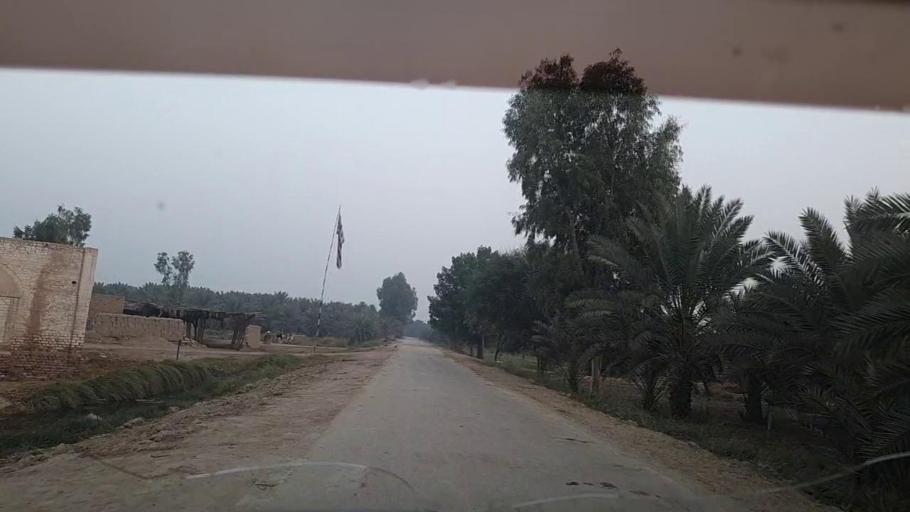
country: PK
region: Sindh
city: Khairpur
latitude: 27.5752
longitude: 68.7226
